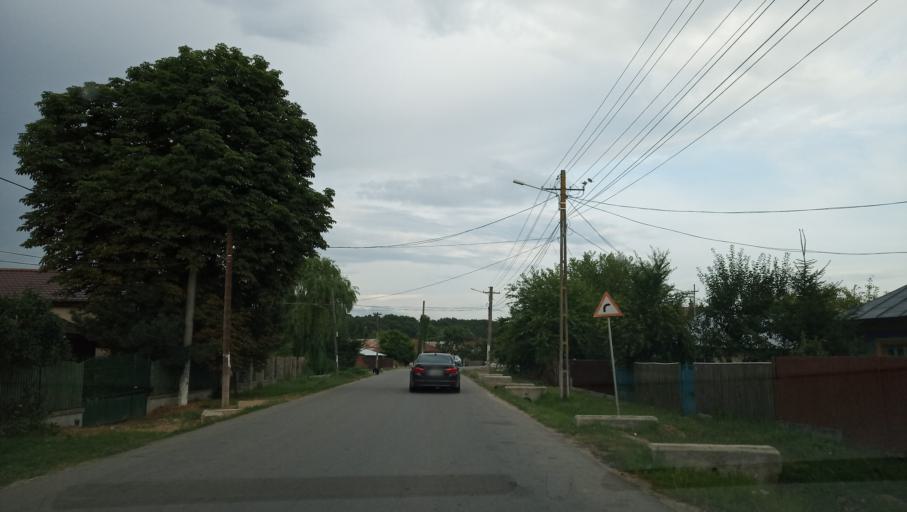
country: RO
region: Giurgiu
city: Iepuresti
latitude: 44.2579
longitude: 25.8845
